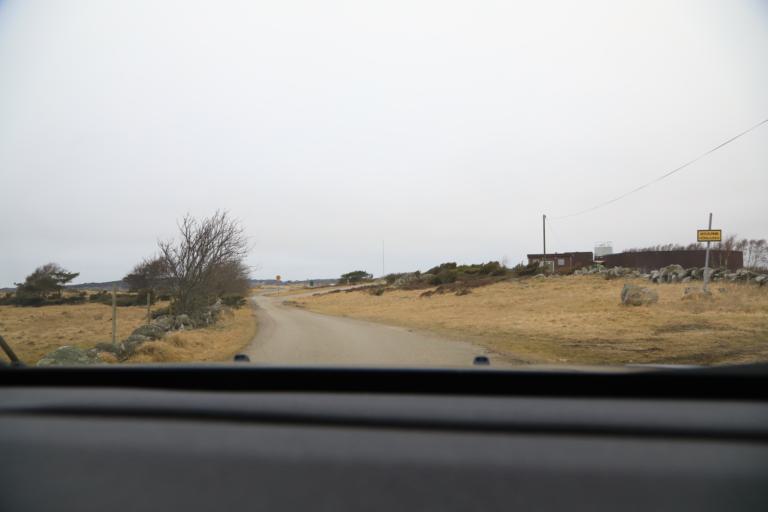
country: SE
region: Halland
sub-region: Kungsbacka Kommun
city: Frillesas
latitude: 57.2428
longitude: 12.1236
